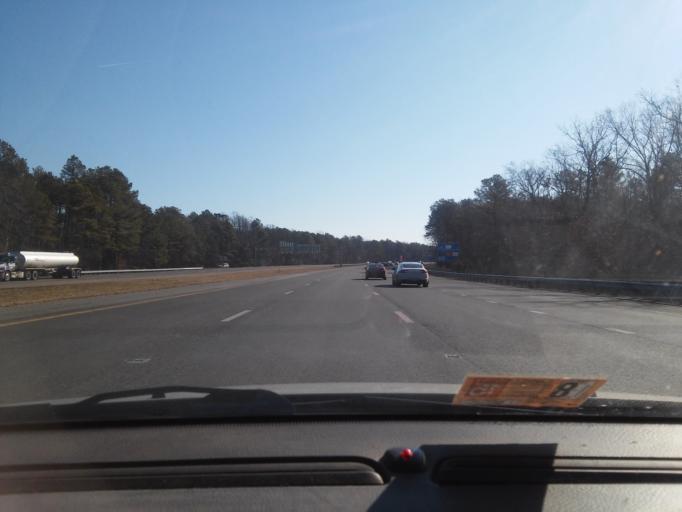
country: US
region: Virginia
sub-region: Henrico County
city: Short Pump
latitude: 37.6550
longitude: -77.6039
